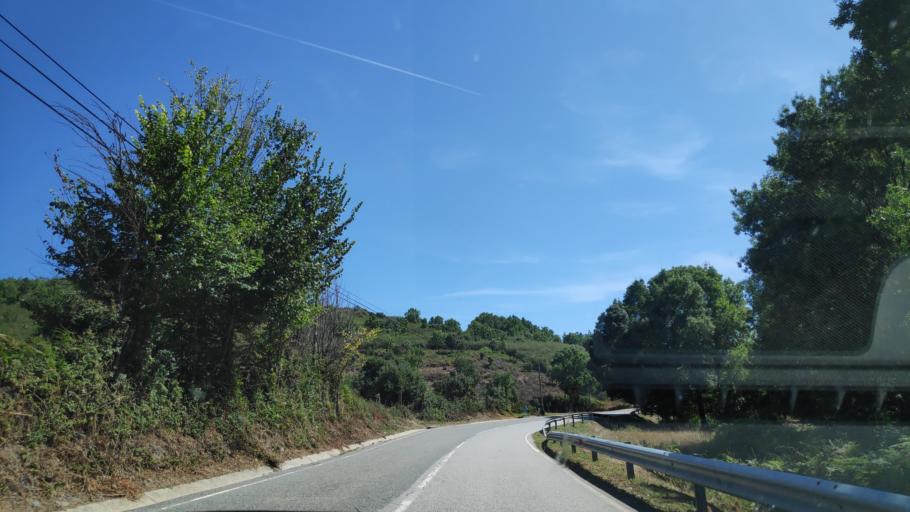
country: PT
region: Braganca
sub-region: Braganca Municipality
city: Braganca
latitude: 41.8879
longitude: -6.7350
